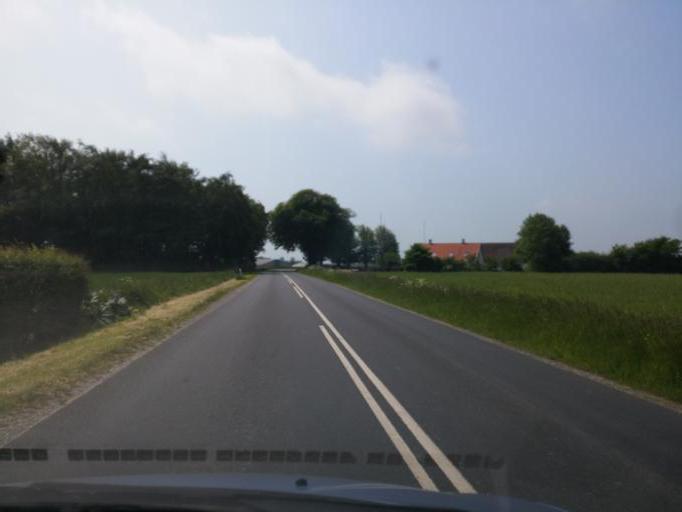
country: DK
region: South Denmark
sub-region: Kerteminde Kommune
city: Kerteminde
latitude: 55.4202
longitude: 10.6126
